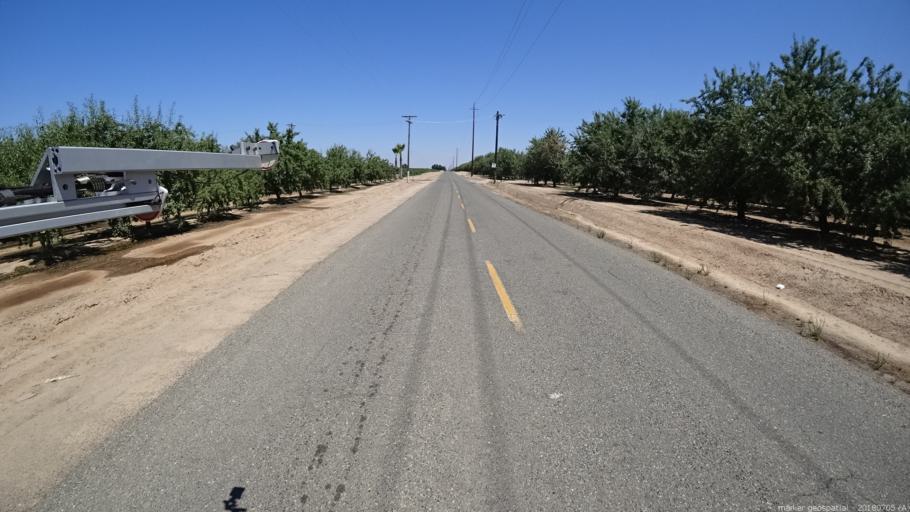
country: US
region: California
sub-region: Madera County
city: Chowchilla
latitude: 37.1557
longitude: -120.2021
